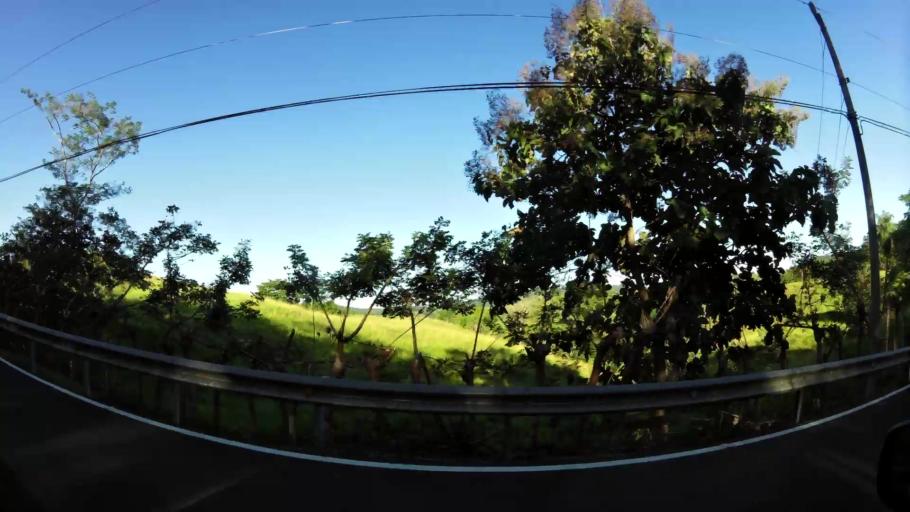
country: CR
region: Puntarenas
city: Miramar
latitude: 10.1493
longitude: -84.8516
